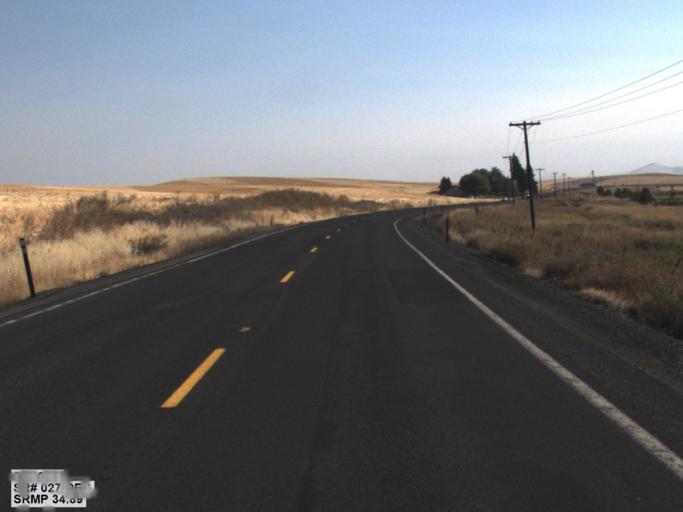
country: US
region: Washington
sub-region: Whitman County
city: Colfax
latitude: 47.1227
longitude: -117.2156
